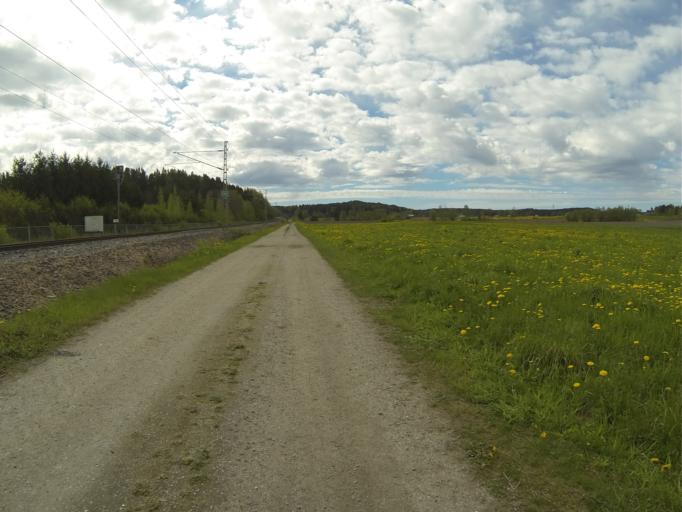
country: FI
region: Varsinais-Suomi
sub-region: Salo
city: Salo
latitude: 60.3662
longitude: 23.1186
